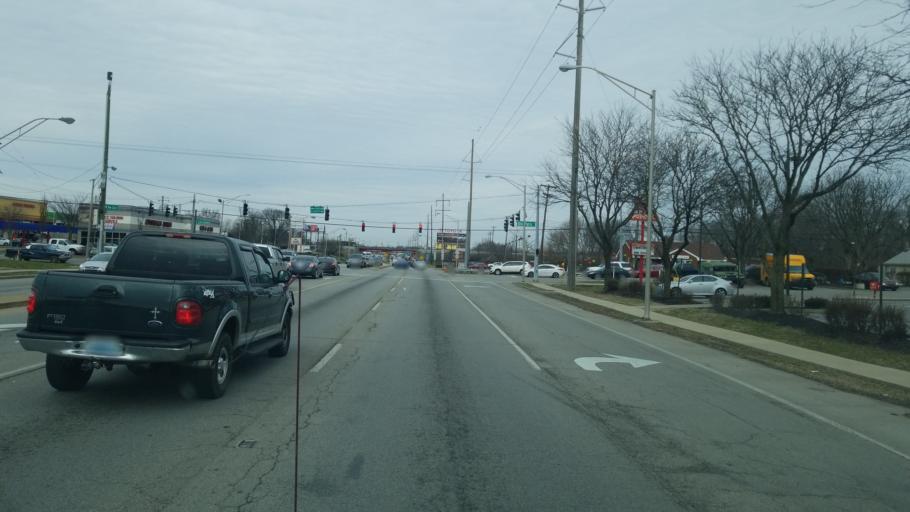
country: US
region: Kentucky
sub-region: Fayette County
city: Lexington-Fayette
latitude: 38.0648
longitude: -84.4695
